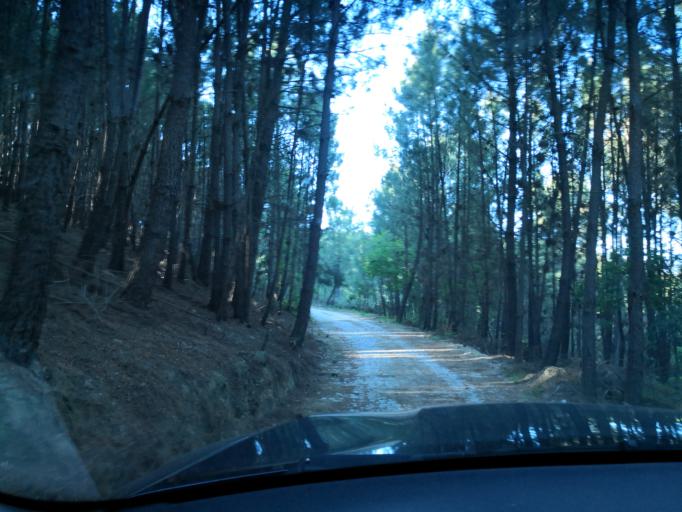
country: PT
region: Vila Real
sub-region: Vila Real
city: Vila Real
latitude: 41.3316
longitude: -7.7476
